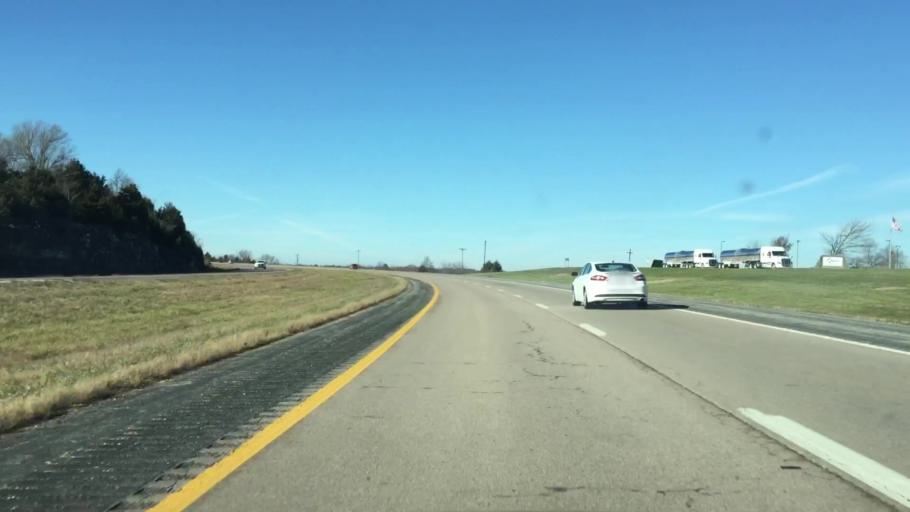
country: US
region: Missouri
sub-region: Miller County
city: Eldon
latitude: 38.3697
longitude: -92.5246
